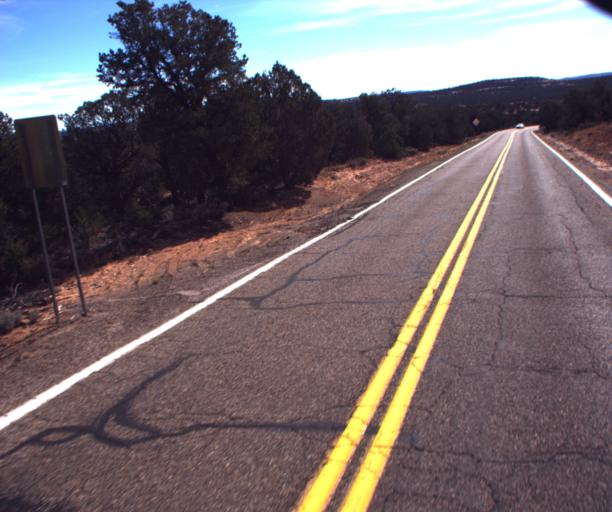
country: US
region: Arizona
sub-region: Navajo County
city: Kayenta
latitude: 36.6656
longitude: -110.5284
